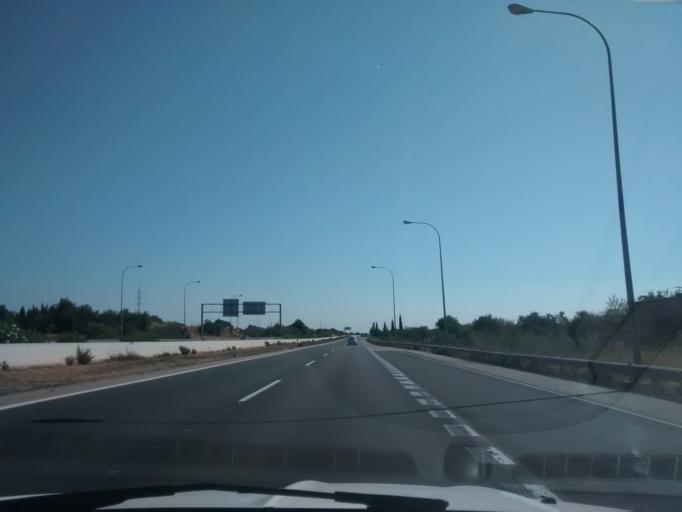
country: ES
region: Balearic Islands
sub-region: Illes Balears
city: Consell
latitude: 39.6703
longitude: 2.8267
